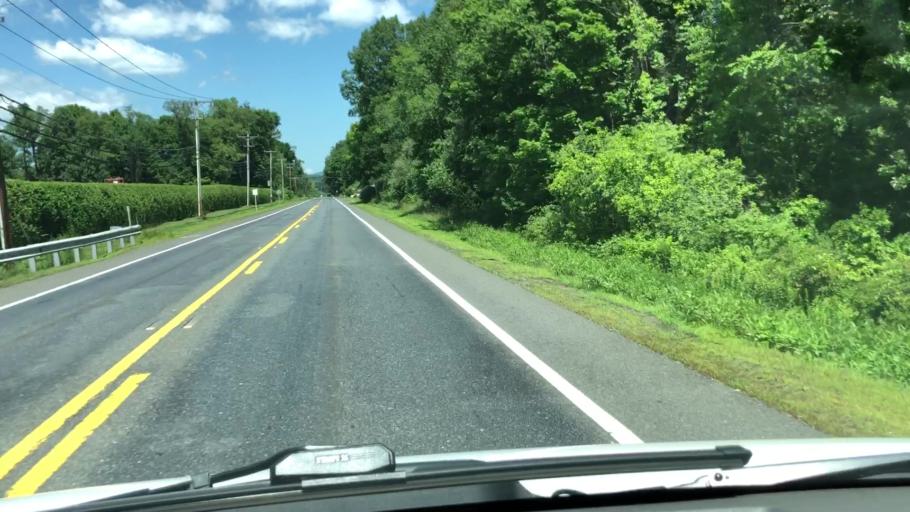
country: US
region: Massachusetts
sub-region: Franklin County
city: Greenfield
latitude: 42.5443
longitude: -72.6016
